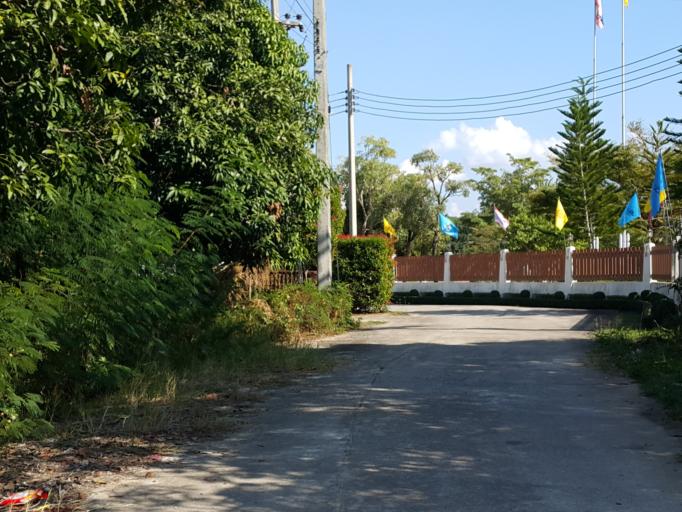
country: TH
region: Chiang Mai
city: San Kamphaeng
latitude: 18.7999
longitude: 99.0974
